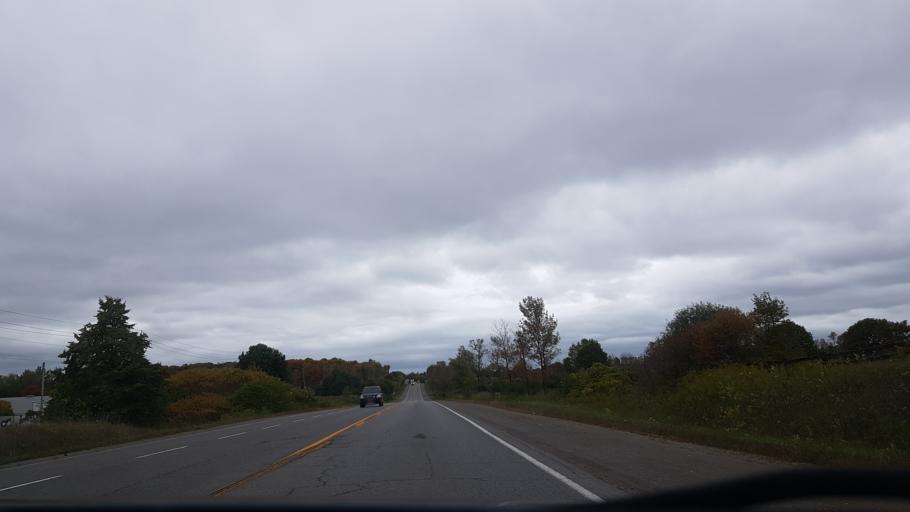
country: CA
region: Ontario
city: Peterborough
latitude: 44.2572
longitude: -78.3941
